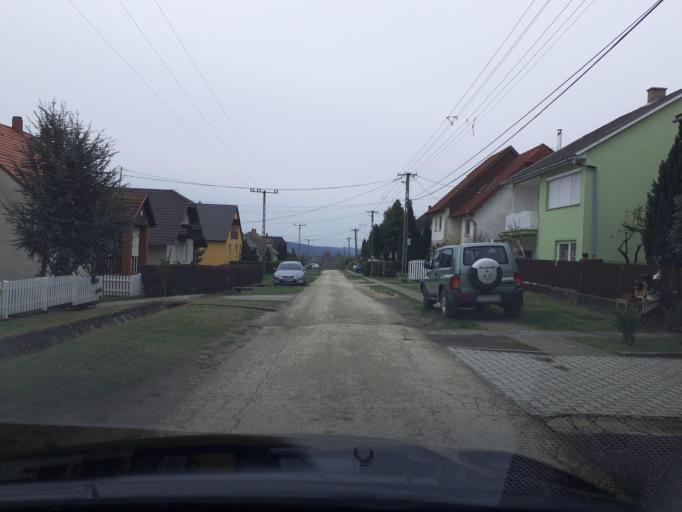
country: HU
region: Tolna
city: Hogyesz
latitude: 46.4999
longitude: 18.4113
